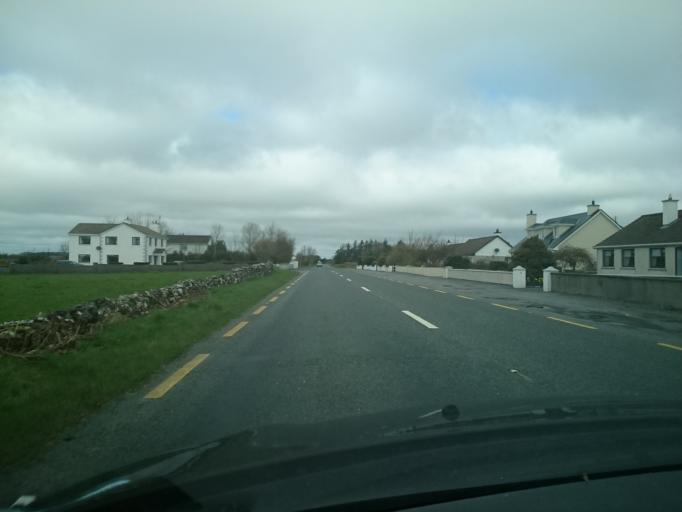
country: IE
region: Connaught
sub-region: Maigh Eo
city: Claremorris
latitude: 53.7524
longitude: -9.0310
